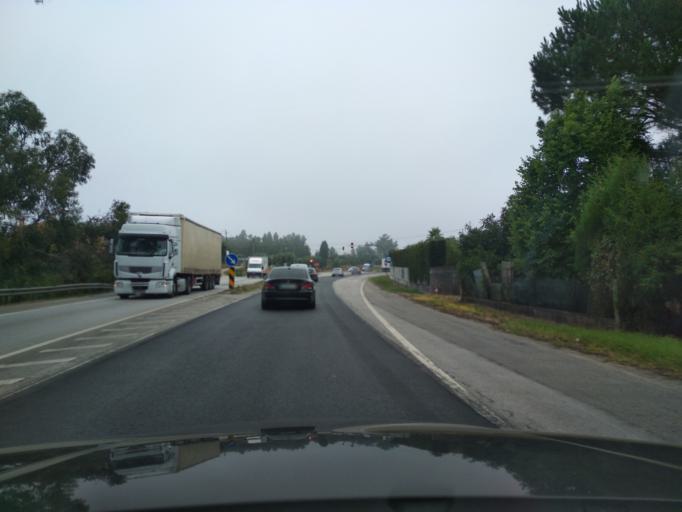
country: PT
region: Aveiro
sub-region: Mealhada
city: Pampilhosa do Botao
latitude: 40.3218
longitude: -8.4550
